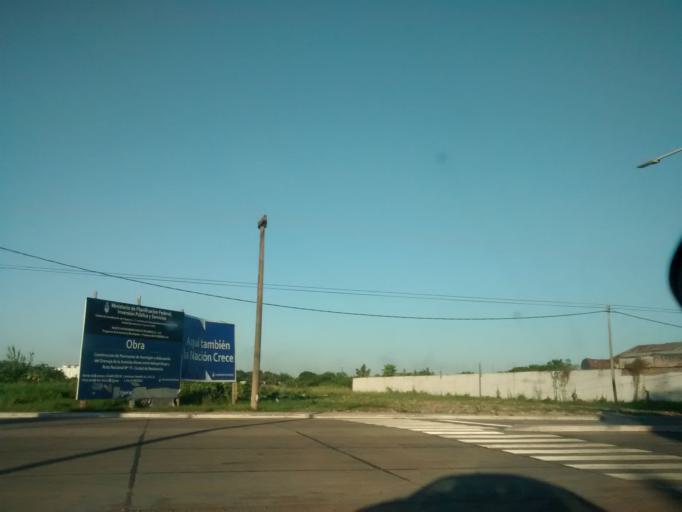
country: AR
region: Chaco
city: Fontana
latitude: -27.4325
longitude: -59.0221
